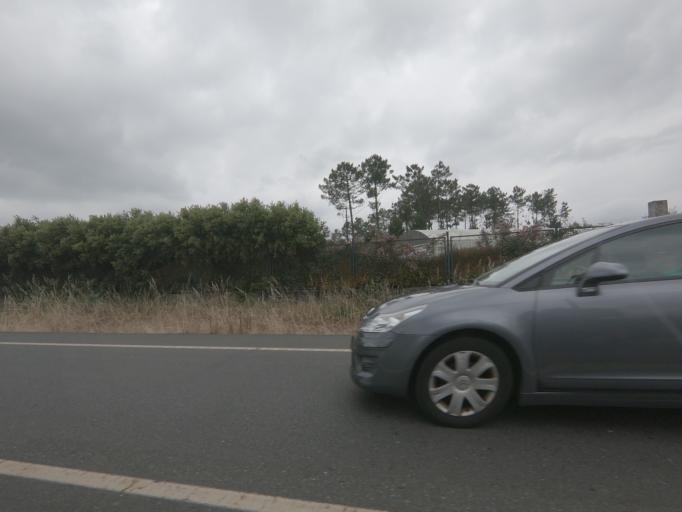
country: ES
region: Galicia
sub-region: Provincia de Pontevedra
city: Tomino
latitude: 41.9914
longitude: -8.7101
